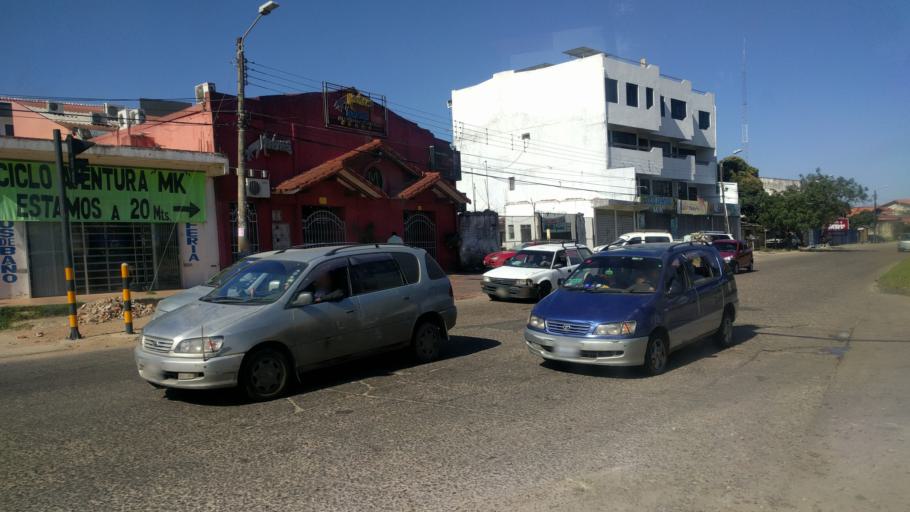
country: BO
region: Santa Cruz
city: Santa Cruz de la Sierra
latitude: -17.7522
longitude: -63.1913
